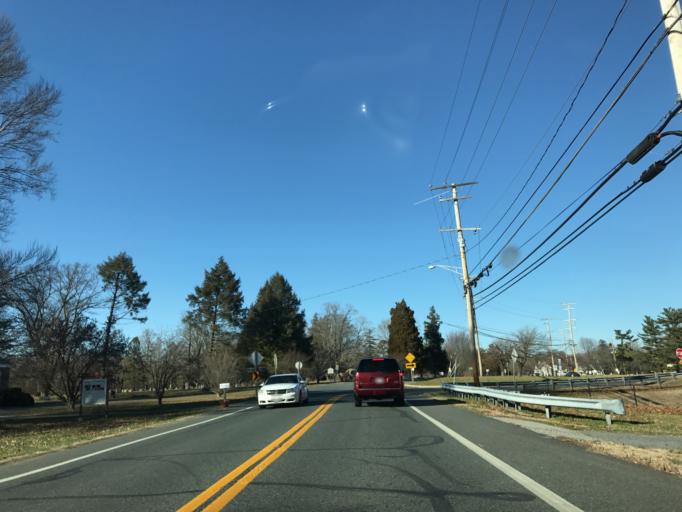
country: US
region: Maryland
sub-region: Harford County
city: Perryman
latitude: 39.4723
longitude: -76.2041
